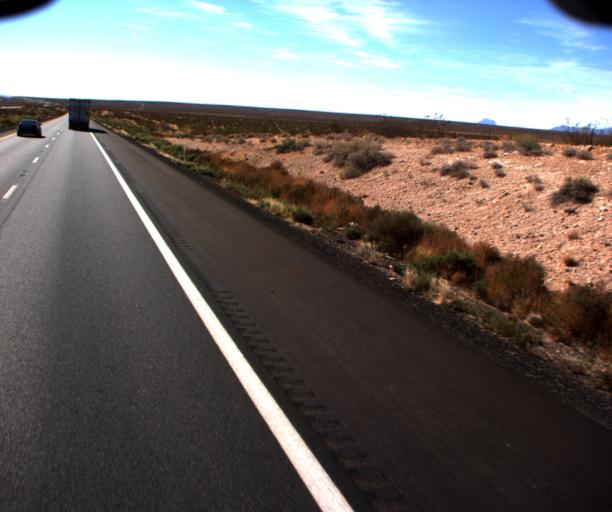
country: US
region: Arizona
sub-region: Mohave County
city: Beaver Dam
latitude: 36.8716
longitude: -113.9617
